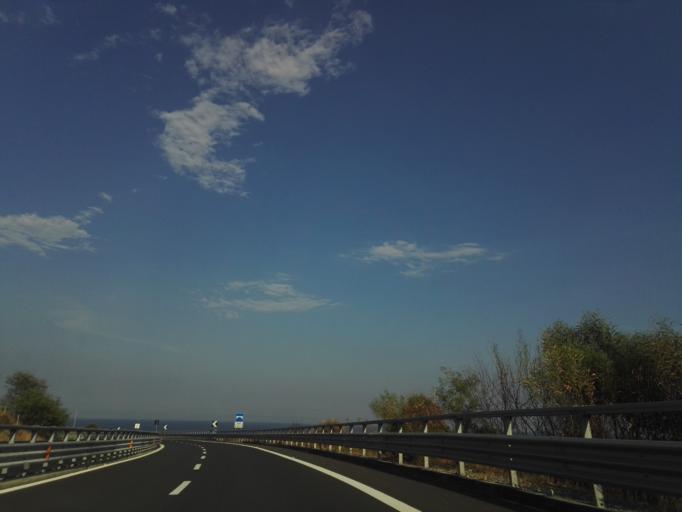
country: IT
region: Calabria
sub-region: Provincia di Reggio Calabria
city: Roccella Ionica
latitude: 38.3283
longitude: 16.4157
